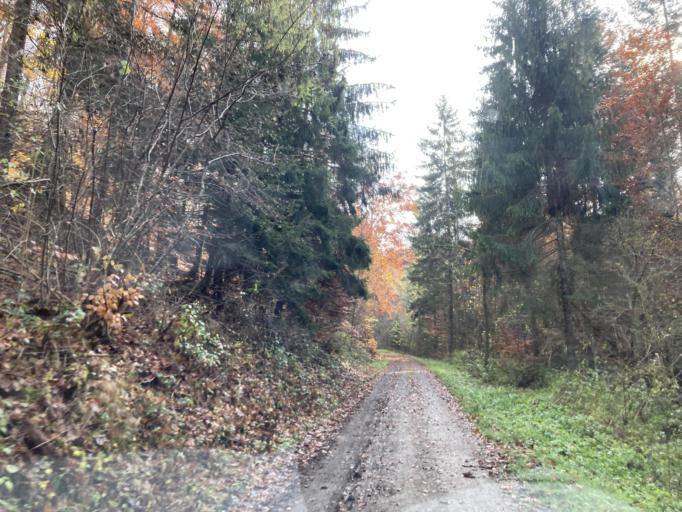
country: DE
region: Baden-Wuerttemberg
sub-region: Regierungsbezirk Stuttgart
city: Bondorf
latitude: 48.4784
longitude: 8.8287
